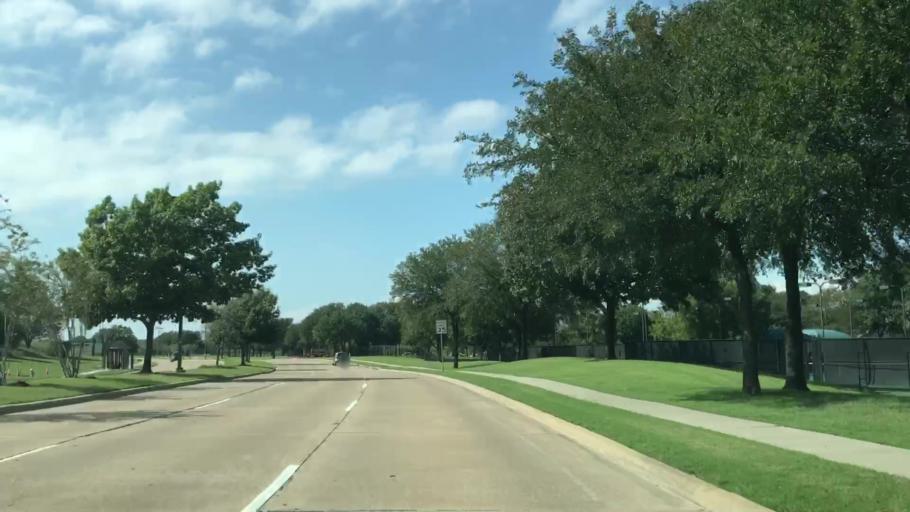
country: US
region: Texas
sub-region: Dallas County
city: Coppell
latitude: 32.9012
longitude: -96.9720
